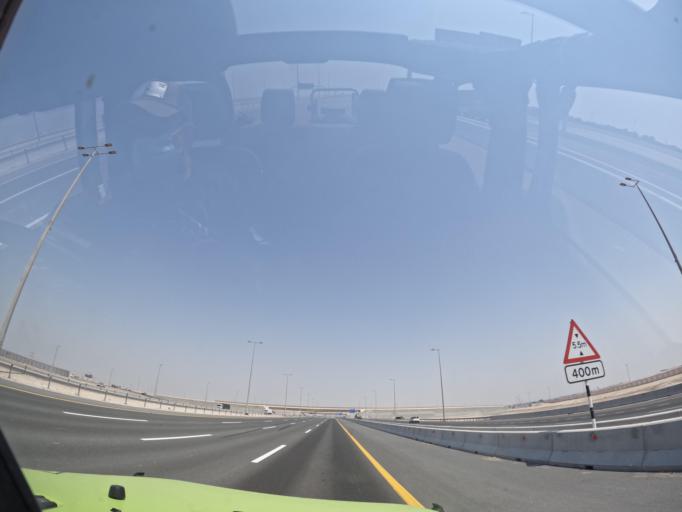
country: AE
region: Abu Dhabi
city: Abu Dhabi
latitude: 24.2849
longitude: 54.5449
